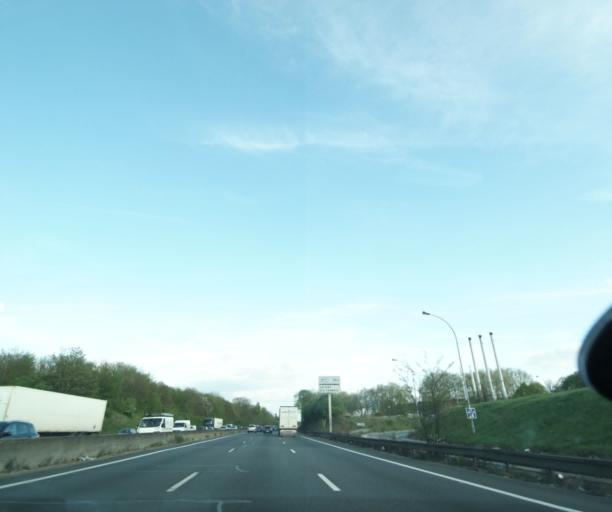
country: FR
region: Ile-de-France
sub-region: Departement de l'Essonne
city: Morsang-sur-Orge
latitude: 48.6594
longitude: 2.3737
